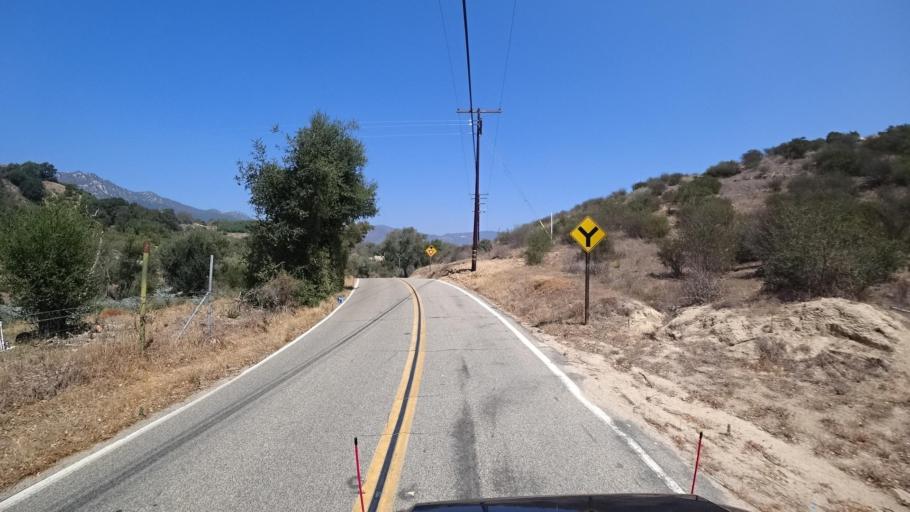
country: US
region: California
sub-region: San Diego County
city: Fallbrook
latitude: 33.4394
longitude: -117.3243
